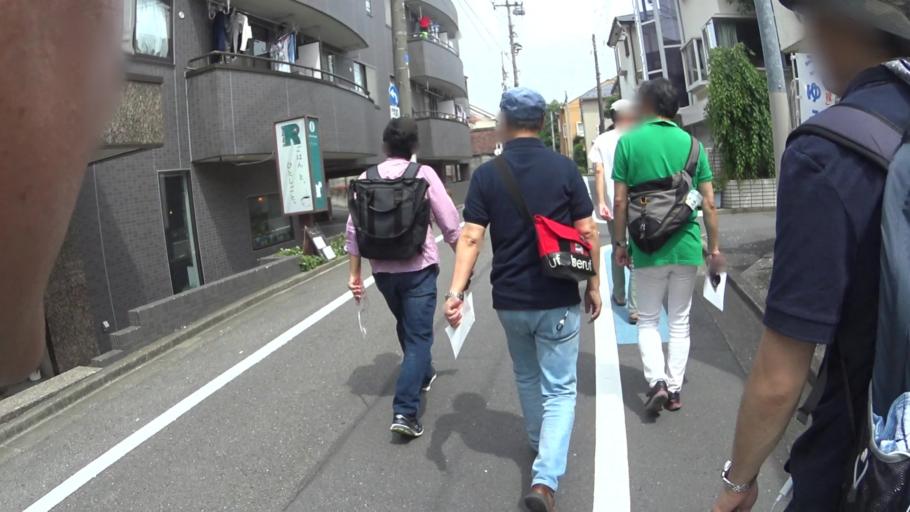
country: JP
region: Tokyo
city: Musashino
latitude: 35.7073
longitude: 139.6028
